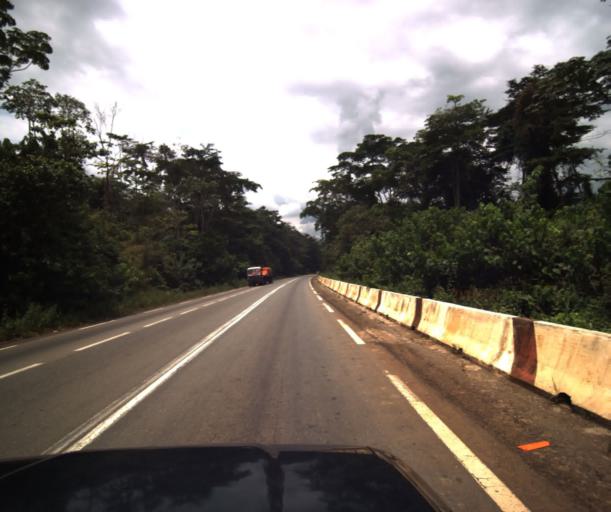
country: CM
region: Centre
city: Eseka
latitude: 3.8743
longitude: 10.8232
